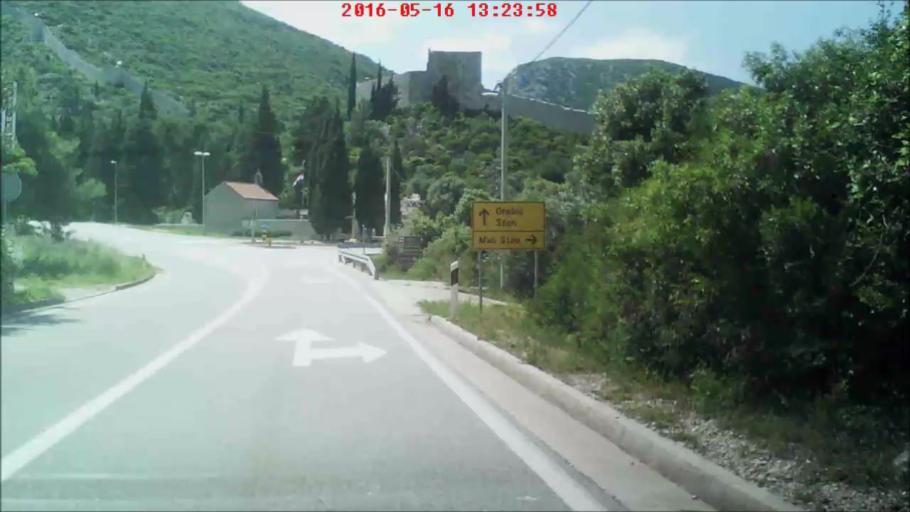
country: HR
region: Dubrovacko-Neretvanska
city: Ston
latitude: 42.8450
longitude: 17.7077
